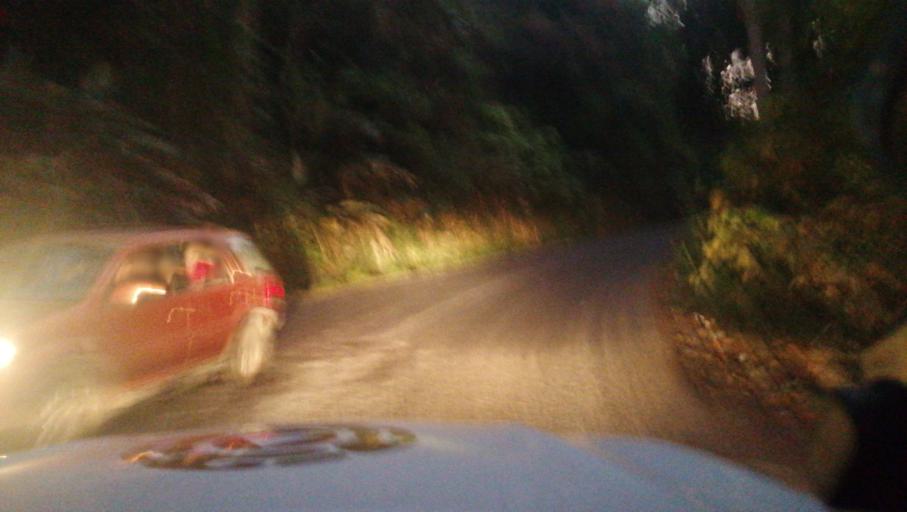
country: MX
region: Chiapas
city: Veinte de Noviembre
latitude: 14.9645
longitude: -92.2522
